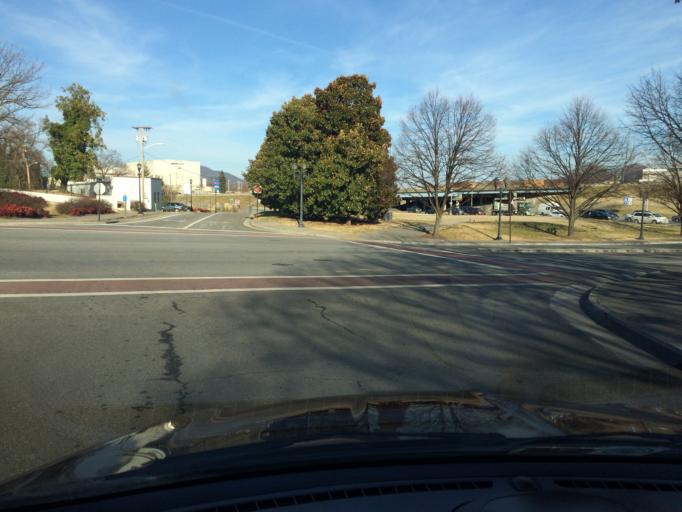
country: US
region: Virginia
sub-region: City of Roanoke
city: Roanoke
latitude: 37.2749
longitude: -79.9379
